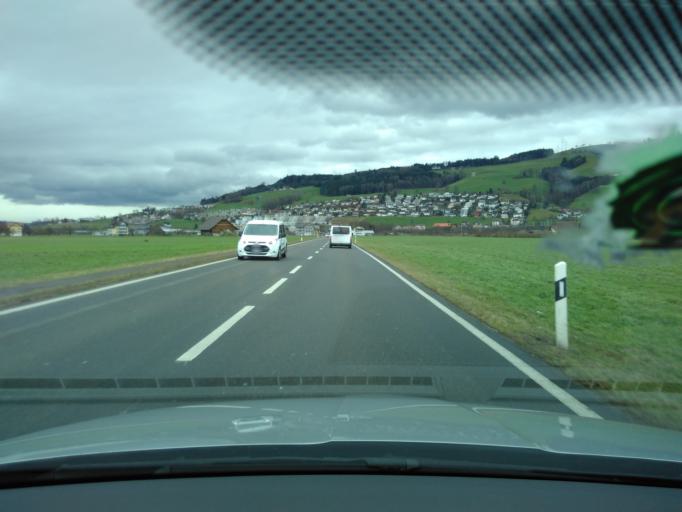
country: CH
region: Lucerne
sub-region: Lucerne-Land District
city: Root
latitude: 47.1247
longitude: 8.3817
